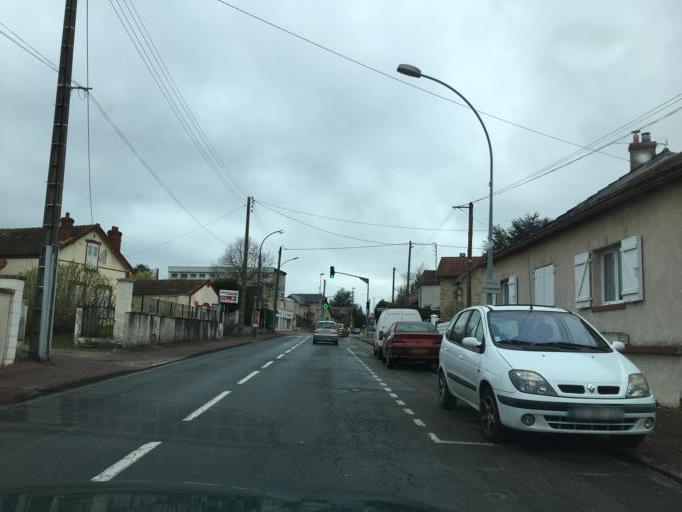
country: FR
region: Centre
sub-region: Departement du Loiret
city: Villemandeur
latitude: 47.9930
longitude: 2.7207
